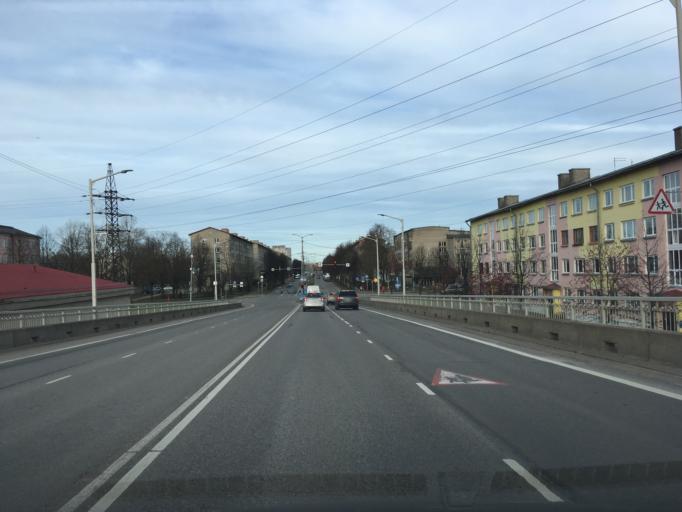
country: EE
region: Ida-Virumaa
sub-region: Narva linn
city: Narva
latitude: 59.3732
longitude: 28.1830
